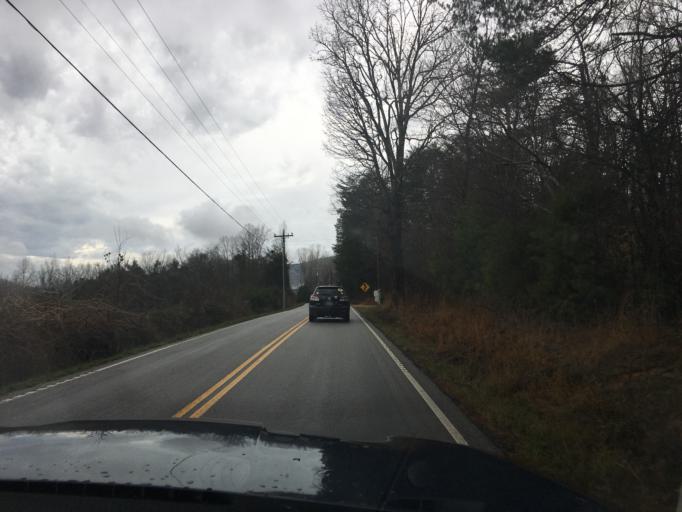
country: US
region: Tennessee
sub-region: McMinn County
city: Englewood
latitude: 35.3431
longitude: -84.3667
